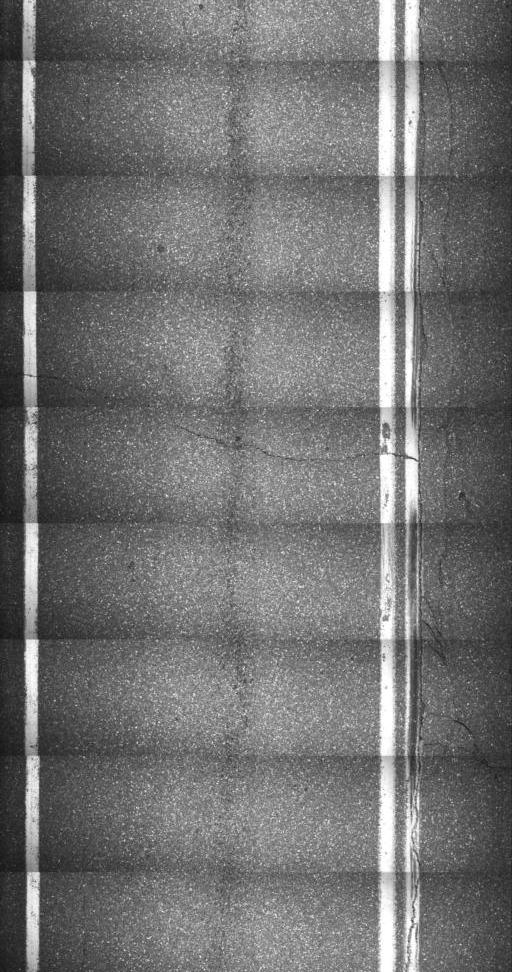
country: US
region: New Hampshire
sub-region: Grafton County
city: Woodsville
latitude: 44.2279
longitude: -72.2290
